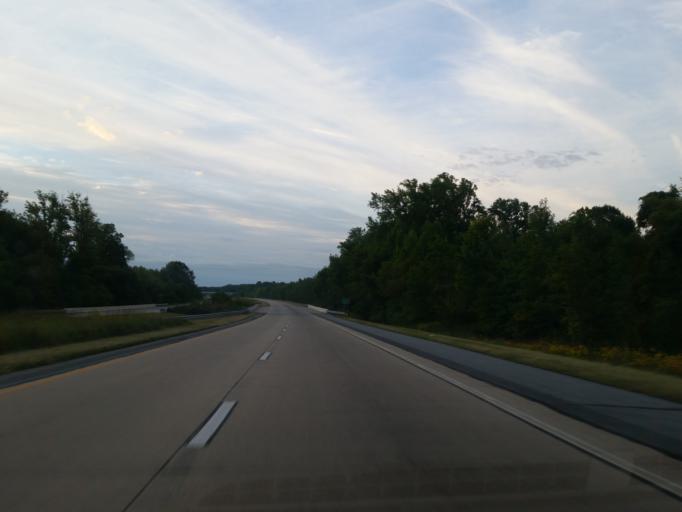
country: US
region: Delaware
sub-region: Kent County
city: Cheswold
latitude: 39.2351
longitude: -75.5796
